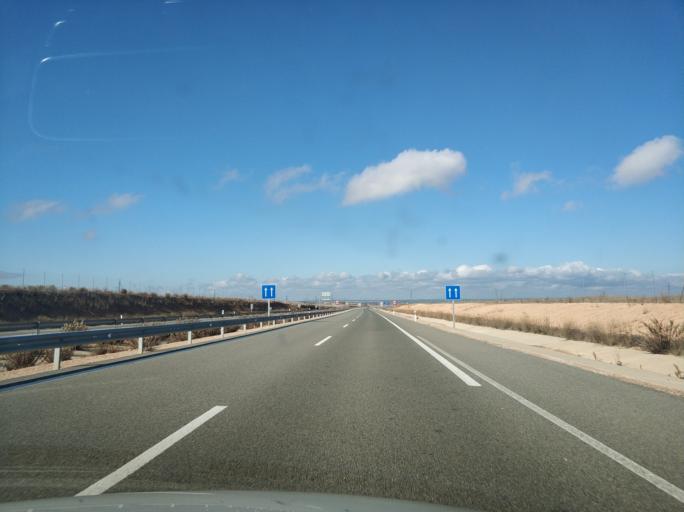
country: ES
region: Castille and Leon
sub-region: Provincia de Soria
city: Coscurita
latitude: 41.4253
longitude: -2.4921
